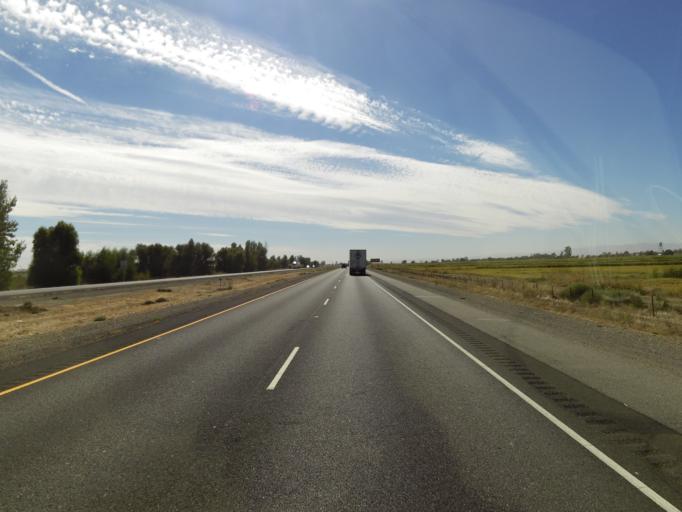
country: US
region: California
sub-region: Colusa County
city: Maxwell
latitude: 39.2898
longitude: -122.1849
